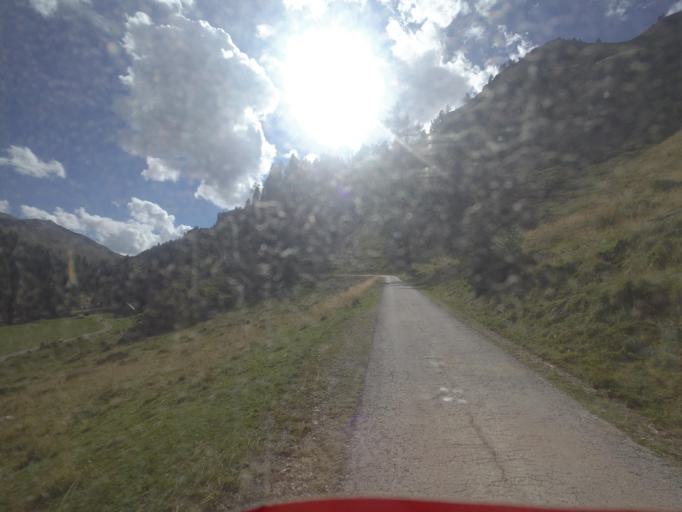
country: AT
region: Salzburg
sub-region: Politischer Bezirk Sankt Johann im Pongau
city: Kleinarl
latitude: 47.1844
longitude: 13.3588
